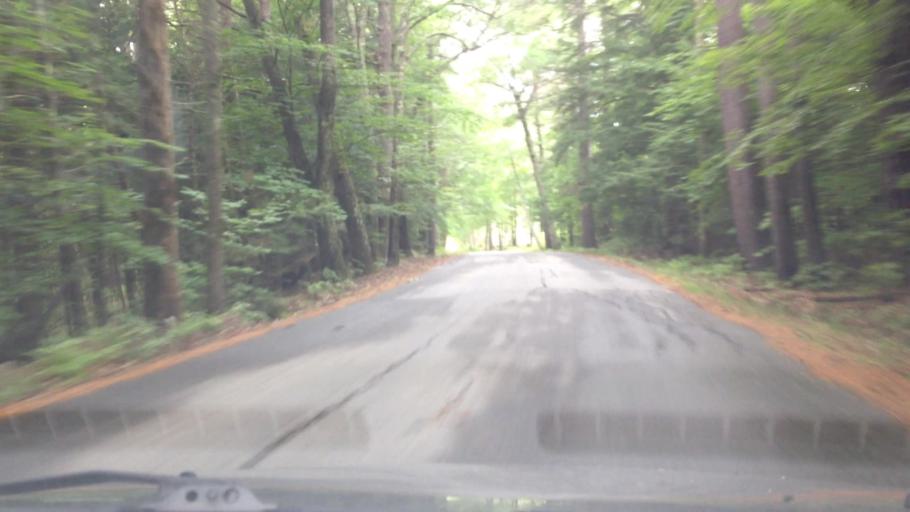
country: US
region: New Hampshire
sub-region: Cheshire County
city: Marlborough
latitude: 42.8961
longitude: -72.1961
